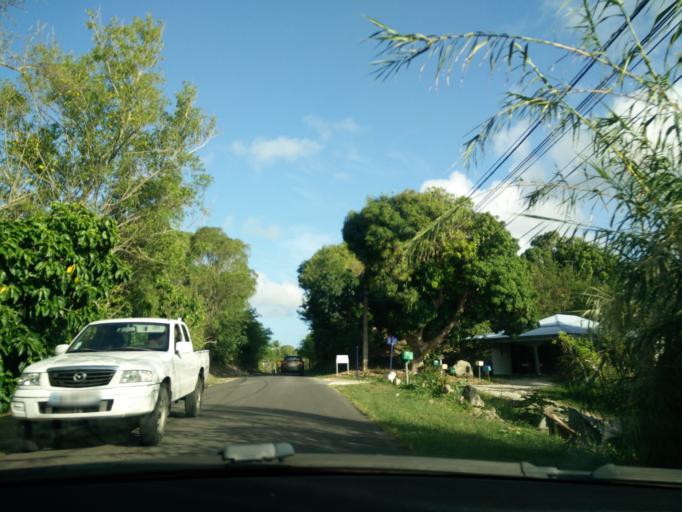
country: GP
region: Guadeloupe
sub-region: Guadeloupe
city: Sainte-Anne
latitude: 16.2770
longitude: -61.3985
